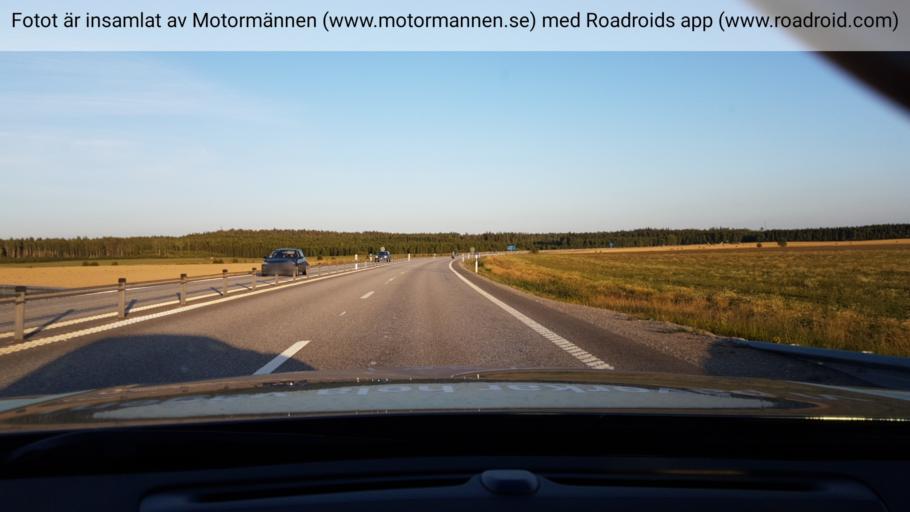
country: SE
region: Vaestmanland
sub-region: Surahammars Kommun
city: Ramnas
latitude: 59.7569
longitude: 16.2159
